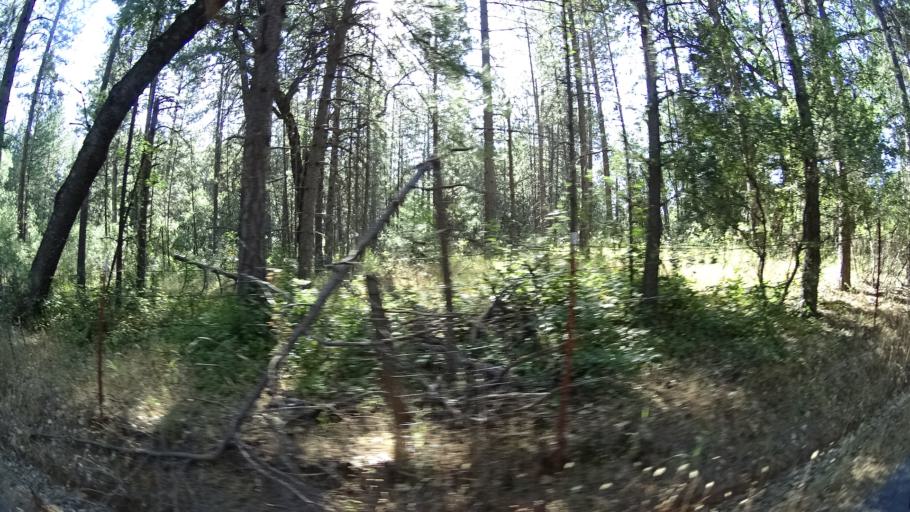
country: US
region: California
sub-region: Amador County
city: Pioneer
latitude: 38.3832
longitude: -120.5557
